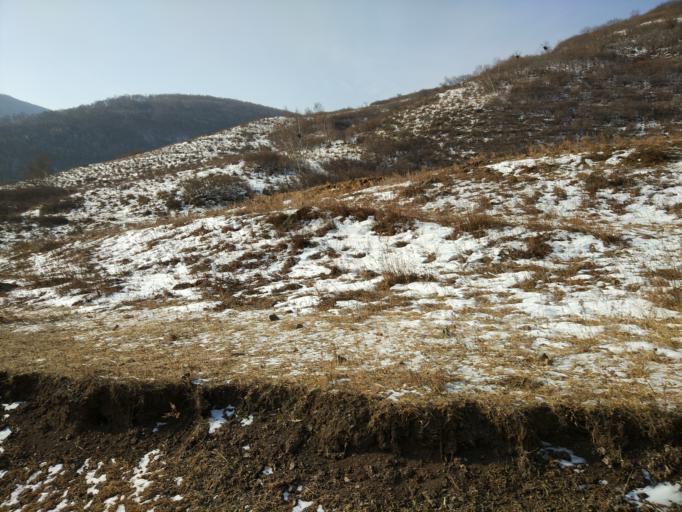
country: CN
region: Hebei
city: Xiwanzi
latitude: 40.8591
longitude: 115.4556
